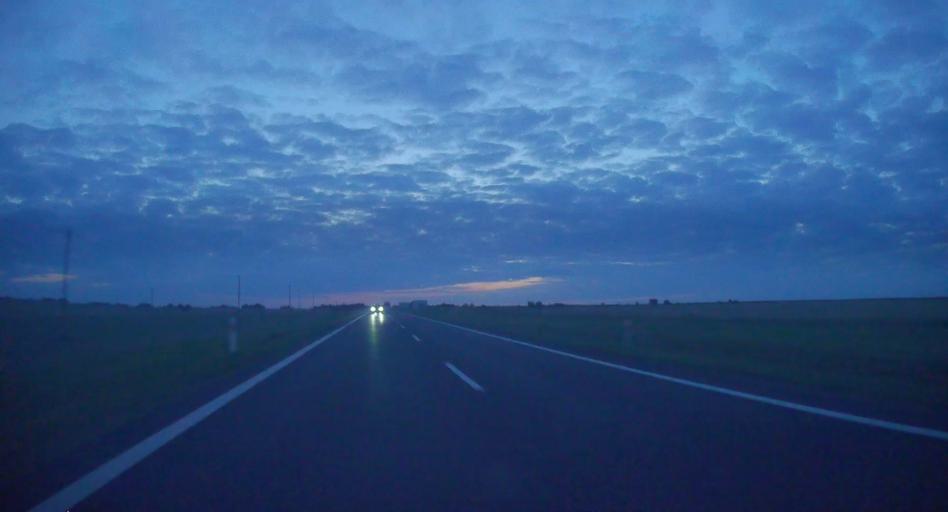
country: PL
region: Silesian Voivodeship
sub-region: Powiat klobucki
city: Klobuck
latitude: 50.8908
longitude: 18.9658
